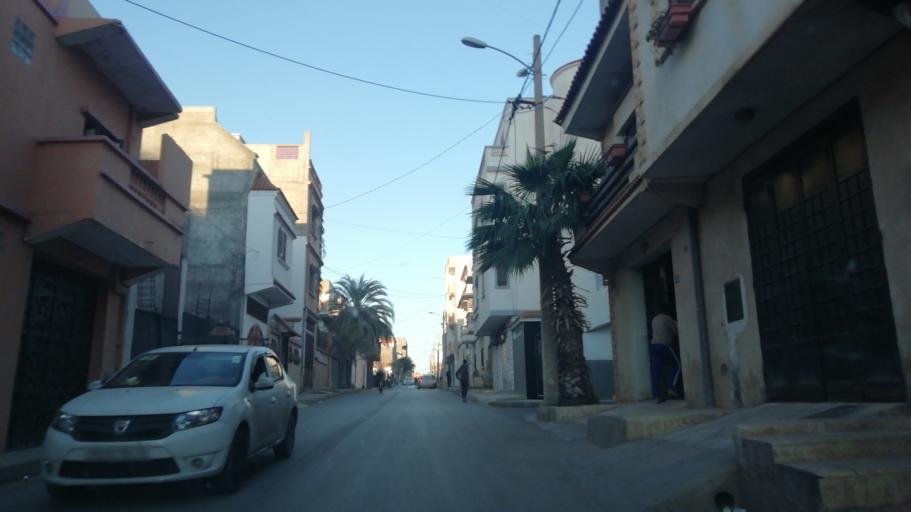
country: DZ
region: Oran
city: Bir el Djir
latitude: 35.7303
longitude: -0.5829
